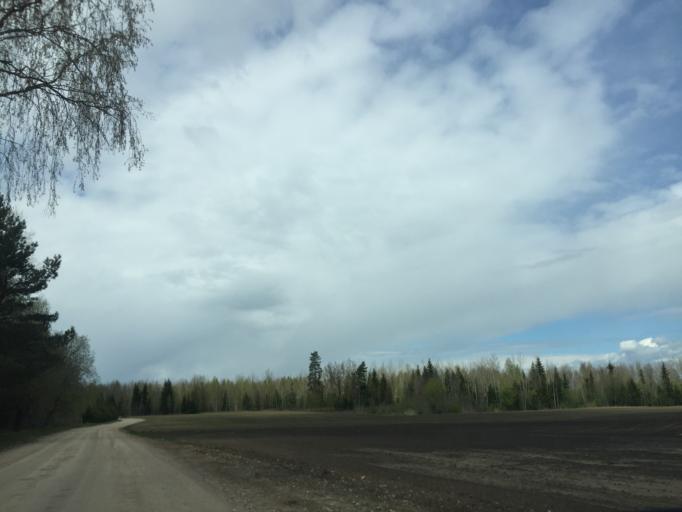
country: LV
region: Lecava
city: Iecava
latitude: 56.6560
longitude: 24.2239
